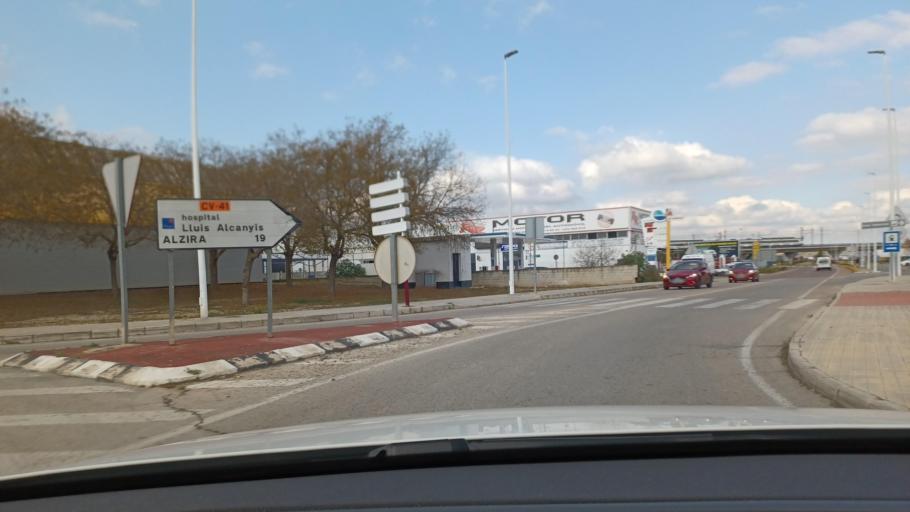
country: ES
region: Valencia
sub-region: Provincia de Valencia
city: Xativa
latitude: 38.9956
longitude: -0.5132
